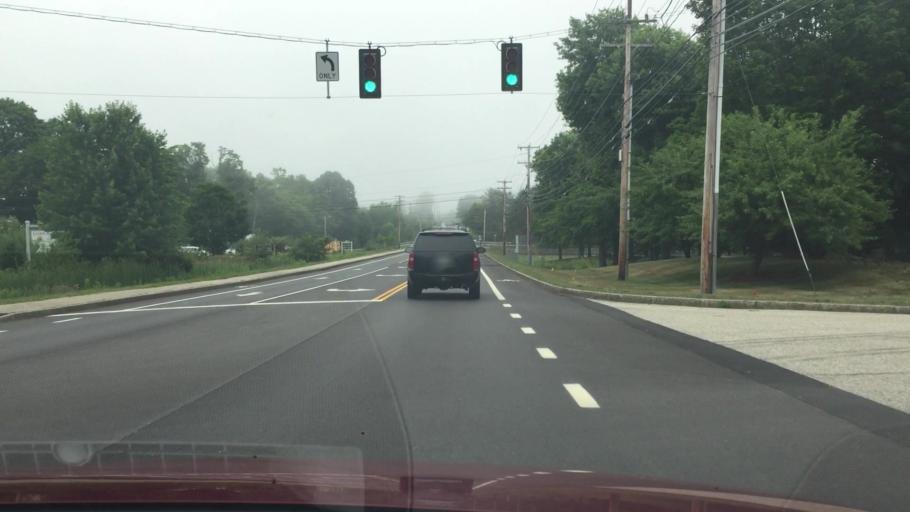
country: US
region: Maine
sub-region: Cumberland County
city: Freeport
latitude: 43.8492
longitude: -70.1116
